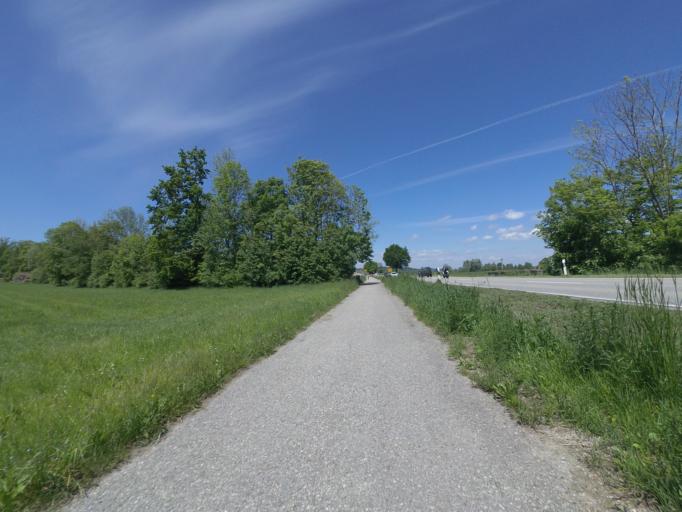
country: DE
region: Bavaria
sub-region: Upper Bavaria
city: Taching am See
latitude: 47.9504
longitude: 12.7346
